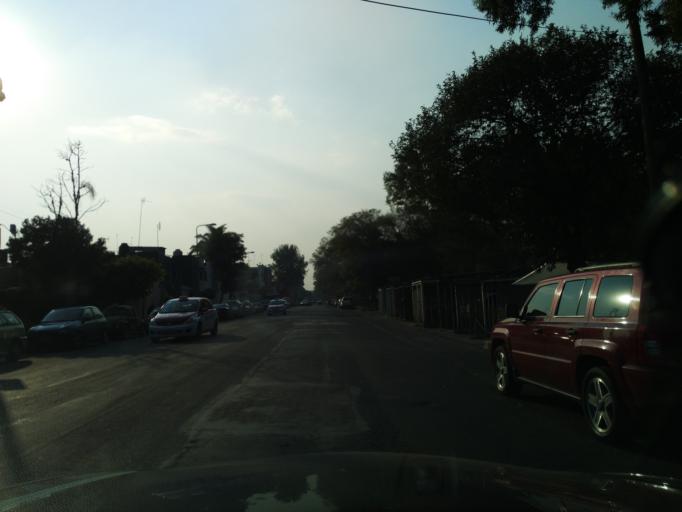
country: MX
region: Mexico City
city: Coyoacan
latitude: 19.3164
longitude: -99.1171
